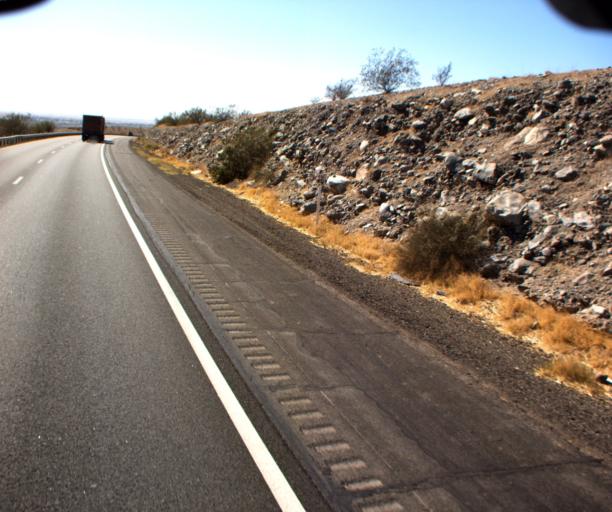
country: US
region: Arizona
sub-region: Yuma County
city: Fortuna Foothills
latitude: 32.6594
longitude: -114.3375
